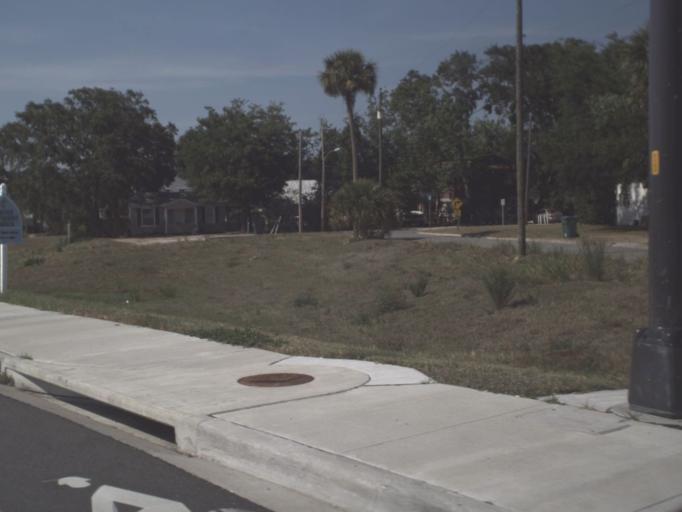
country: US
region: Florida
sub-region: Brevard County
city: Rockledge
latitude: 28.3635
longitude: -80.7346
